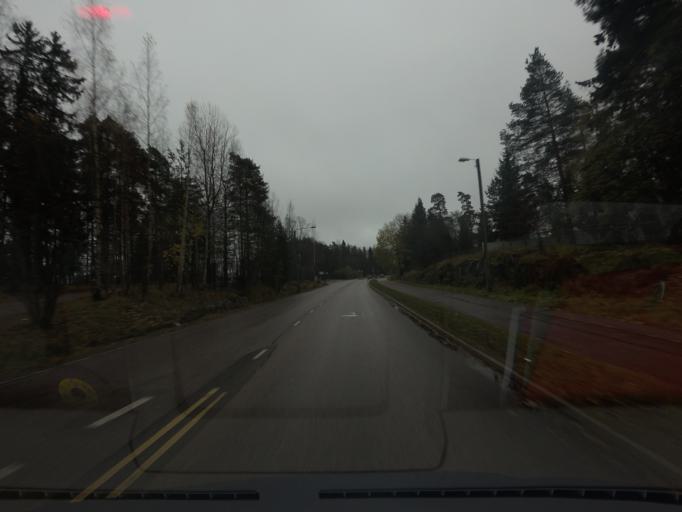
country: FI
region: Uusimaa
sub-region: Helsinki
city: Kilo
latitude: 60.2292
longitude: 24.7783
